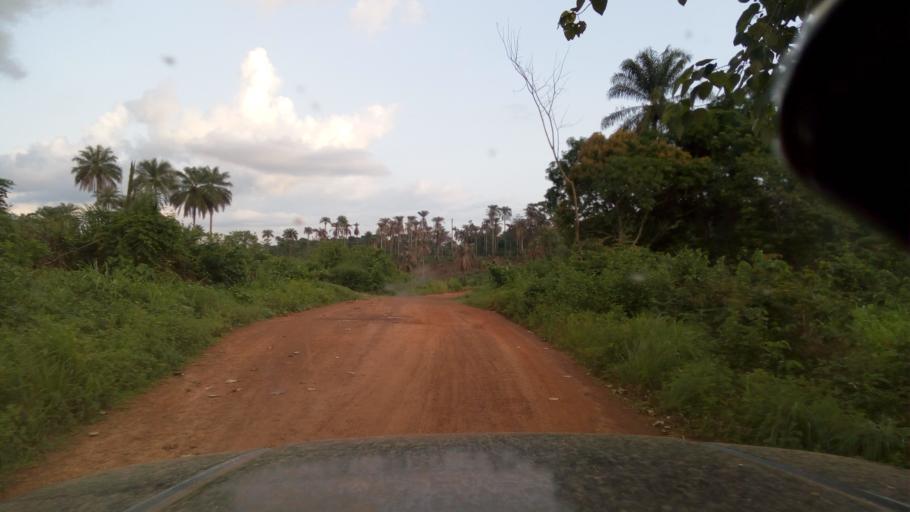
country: SL
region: Eastern Province
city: Gorahun
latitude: 7.5998
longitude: -11.1459
